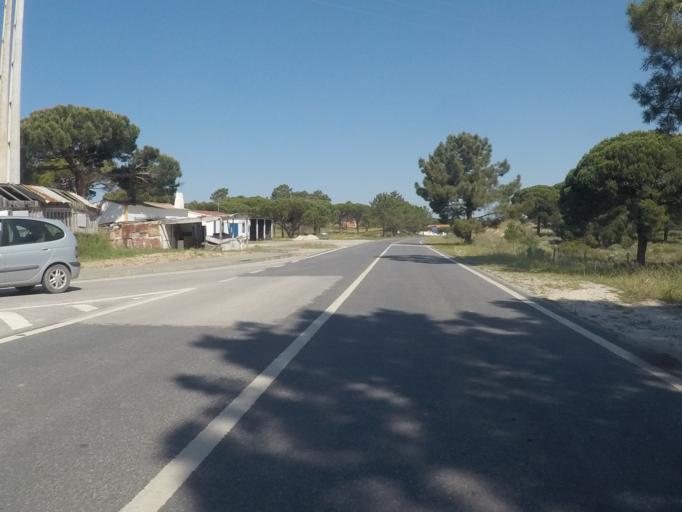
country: PT
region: Setubal
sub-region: Grandola
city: Grandola
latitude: 38.3071
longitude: -8.7400
